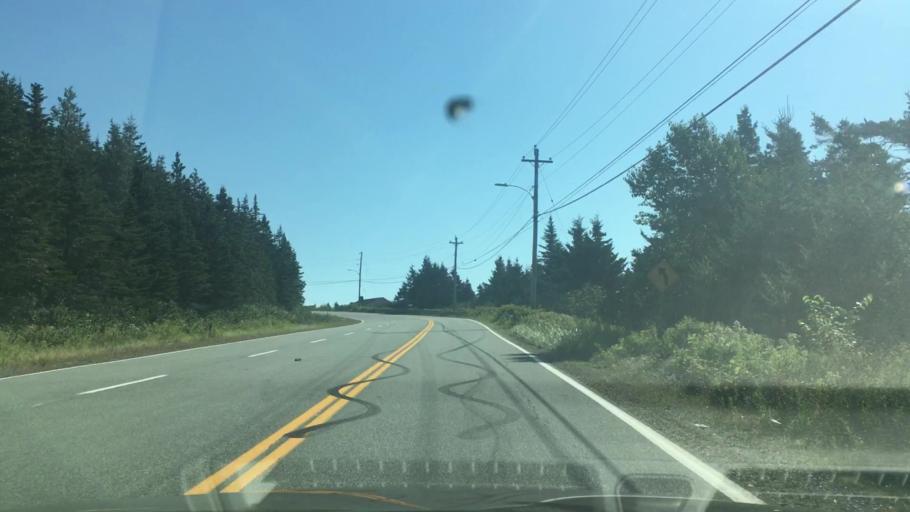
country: CA
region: Nova Scotia
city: New Glasgow
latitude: 44.8141
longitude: -62.6347
